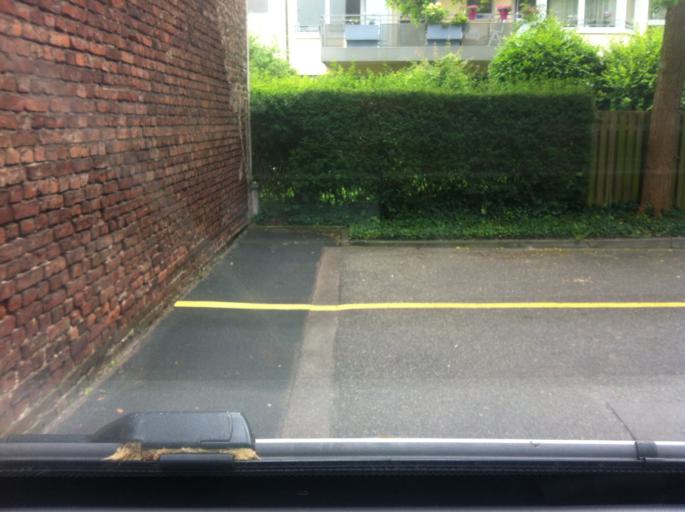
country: DE
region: North Rhine-Westphalia
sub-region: Regierungsbezirk Koln
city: Neuehrenfeld
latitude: 50.9431
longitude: 6.9196
